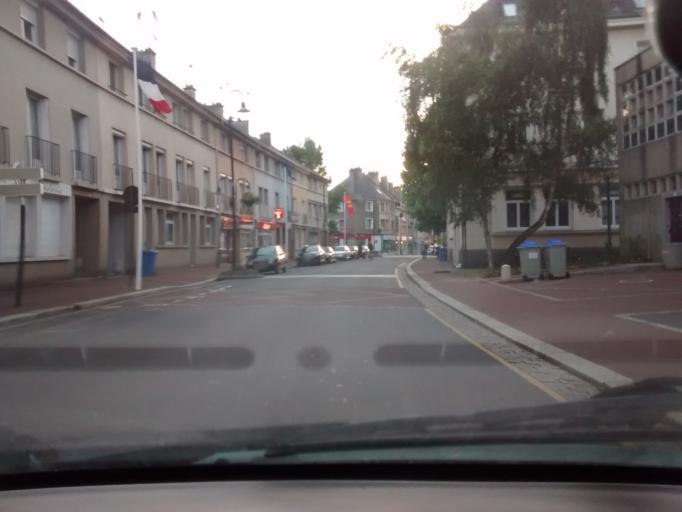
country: FR
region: Lower Normandy
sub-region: Departement de la Manche
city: Saint-Lo
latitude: 49.1137
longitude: -1.0910
